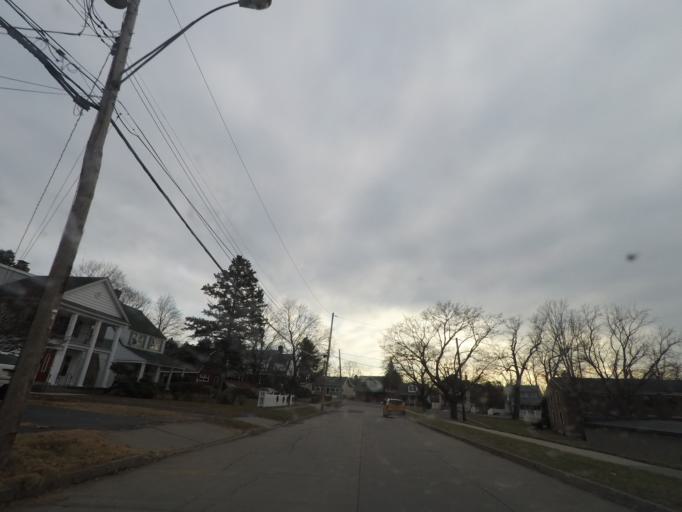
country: US
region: New York
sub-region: Albany County
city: Green Island
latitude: 42.7388
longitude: -73.6681
